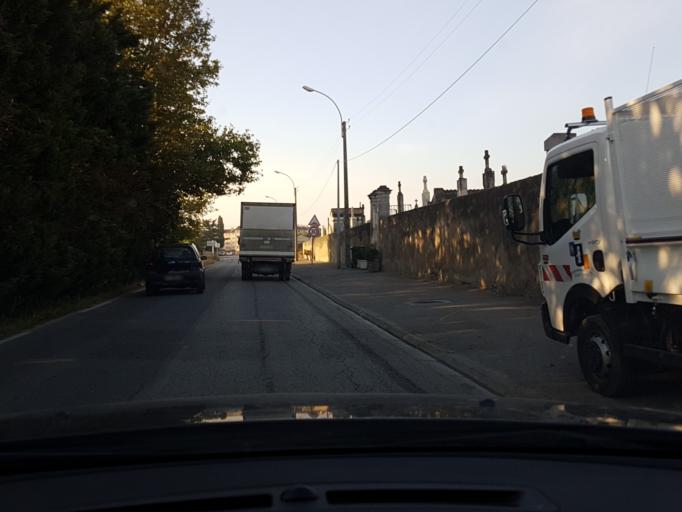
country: FR
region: Provence-Alpes-Cote d'Azur
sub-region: Departement des Bouches-du-Rhone
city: Saint-Andiol
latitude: 43.8337
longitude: 4.9438
